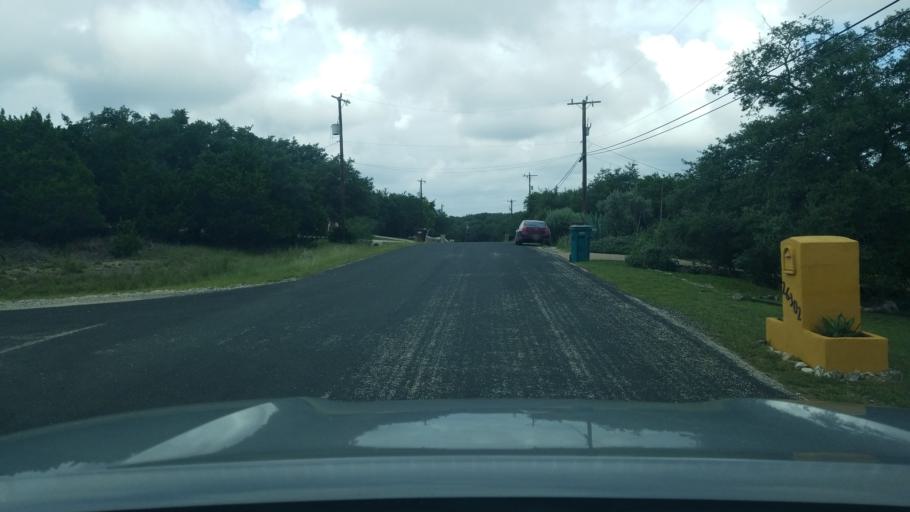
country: US
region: Texas
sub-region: Bexar County
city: Timberwood Park
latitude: 29.6908
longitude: -98.4975
